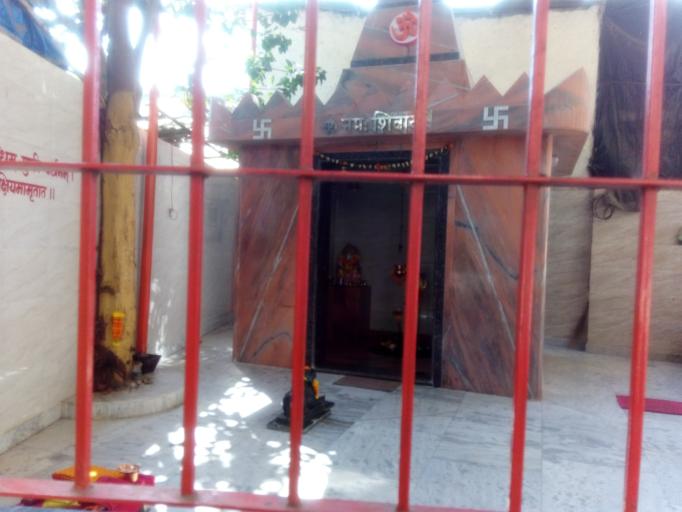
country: IN
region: Maharashtra
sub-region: Mumbai Suburban
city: Mumbai
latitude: 19.0877
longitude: 72.8359
